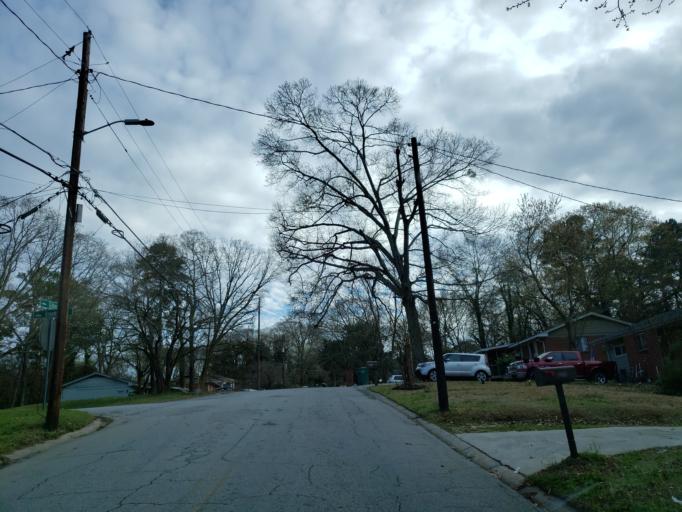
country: US
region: Georgia
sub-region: Clayton County
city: Forest Park
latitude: 33.6379
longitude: -84.3698
